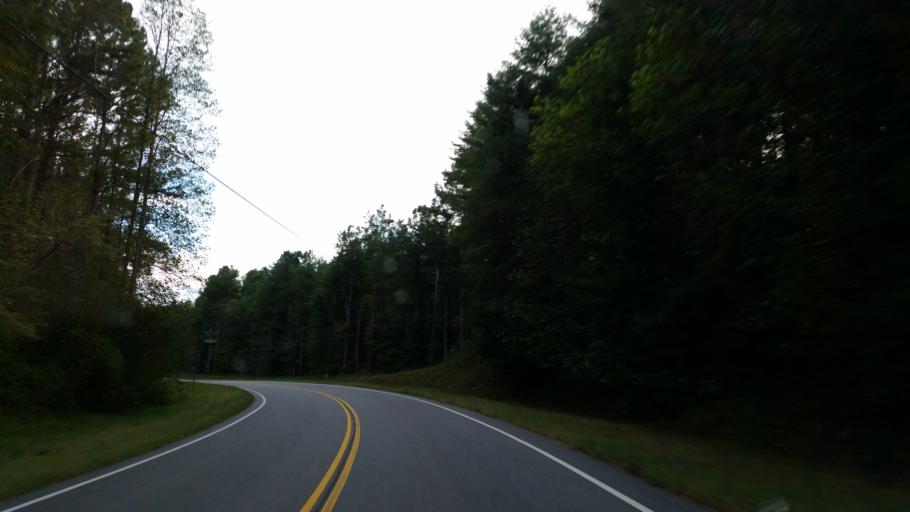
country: US
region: Georgia
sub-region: Lumpkin County
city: Dahlonega
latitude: 34.5179
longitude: -84.0595
